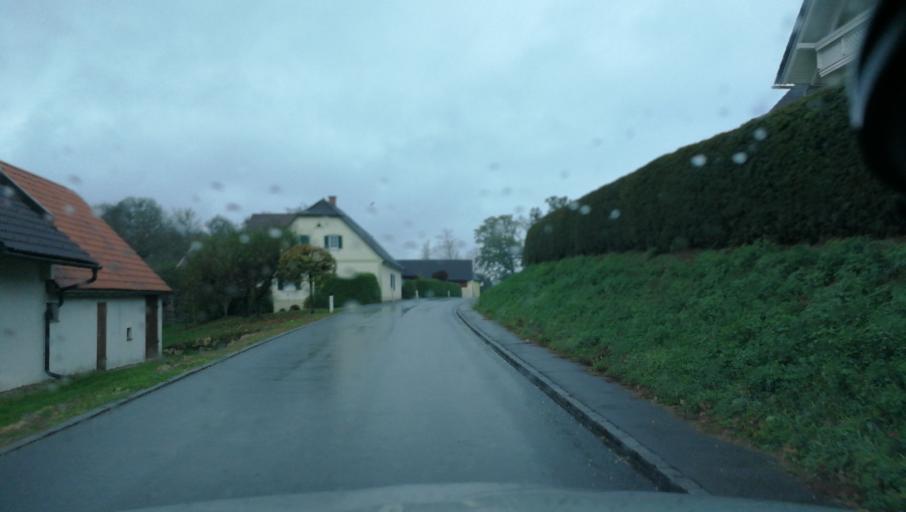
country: AT
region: Styria
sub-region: Politischer Bezirk Leibnitz
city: Strass in Steiermark
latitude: 46.7428
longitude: 15.6364
